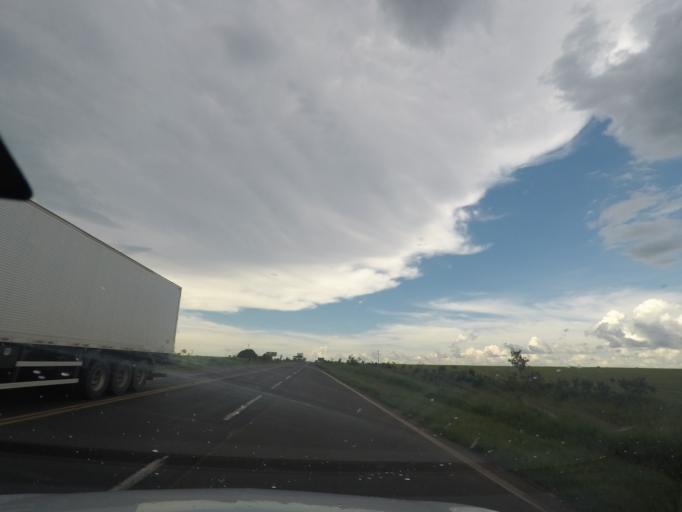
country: BR
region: Minas Gerais
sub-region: Prata
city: Prata
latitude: -19.6291
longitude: -48.8487
